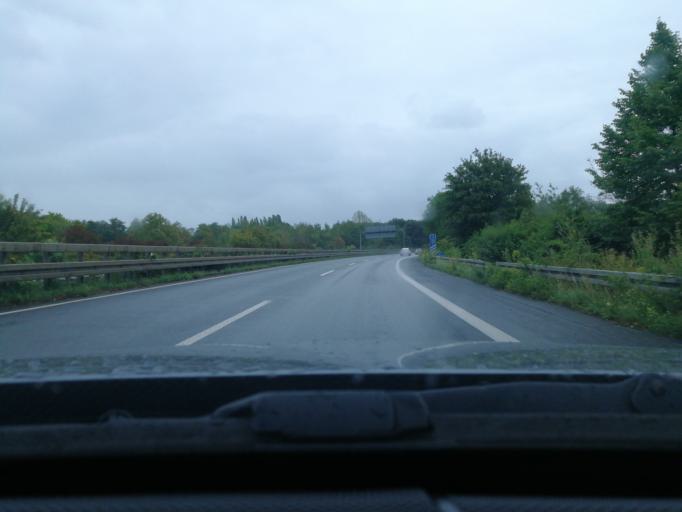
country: DE
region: North Rhine-Westphalia
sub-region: Regierungsbezirk Dusseldorf
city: Dinslaken
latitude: 51.5339
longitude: 6.7546
